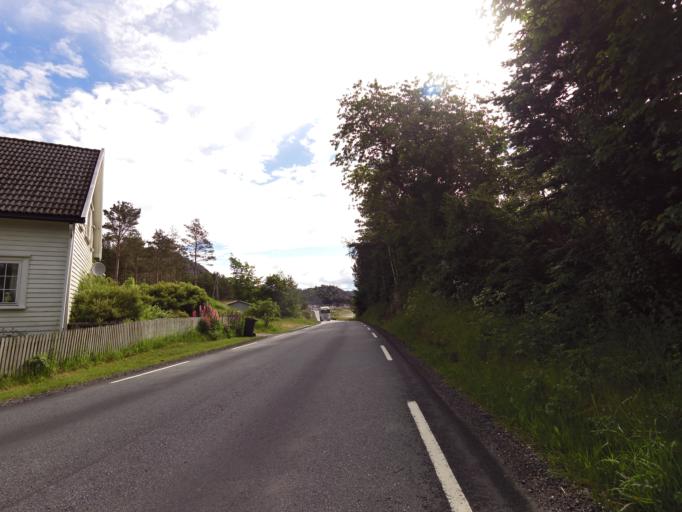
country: NO
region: Vest-Agder
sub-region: Lyngdal
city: Lyngdal
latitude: 58.0459
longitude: 7.1581
